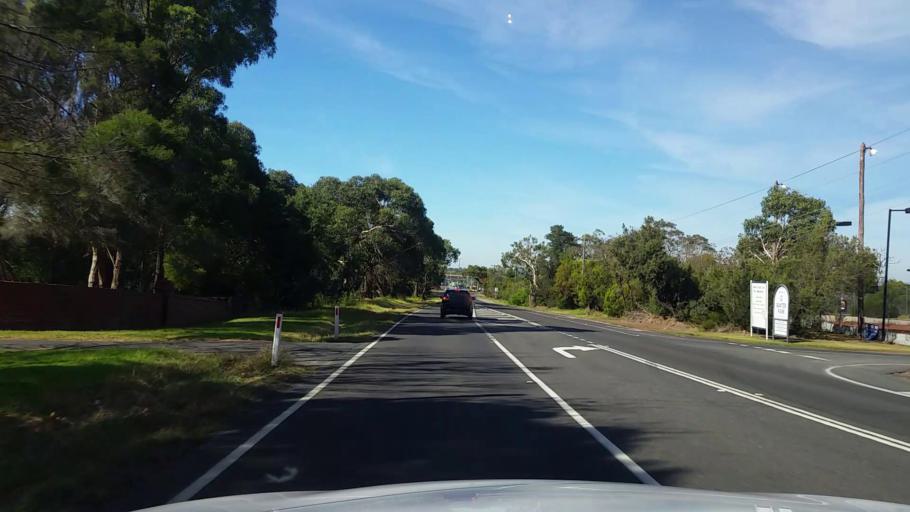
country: AU
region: Victoria
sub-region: Mornington Peninsula
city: Baxter
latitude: -38.1914
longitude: 145.1466
